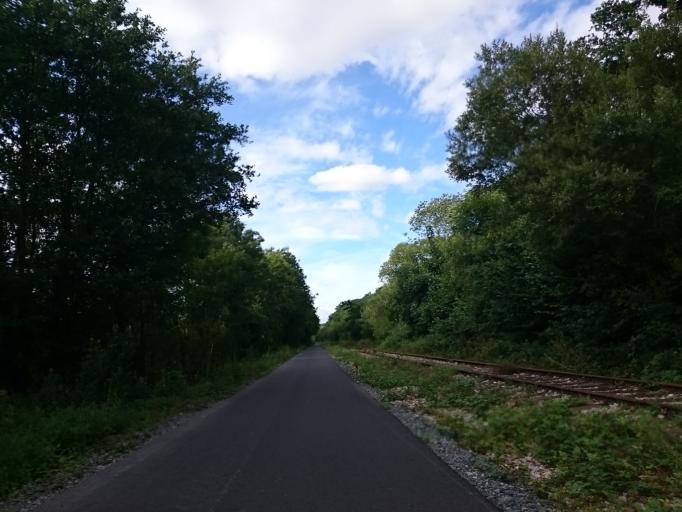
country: FR
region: Lower Normandy
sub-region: Departement du Calvados
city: Clinchamps-sur-Orne
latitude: 49.0784
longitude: -0.4273
